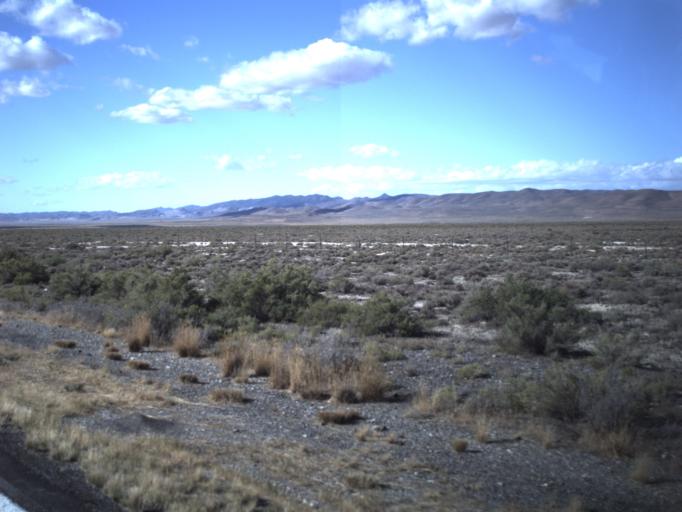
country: US
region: Utah
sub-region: Millard County
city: Delta
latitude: 39.0962
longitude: -112.7492
